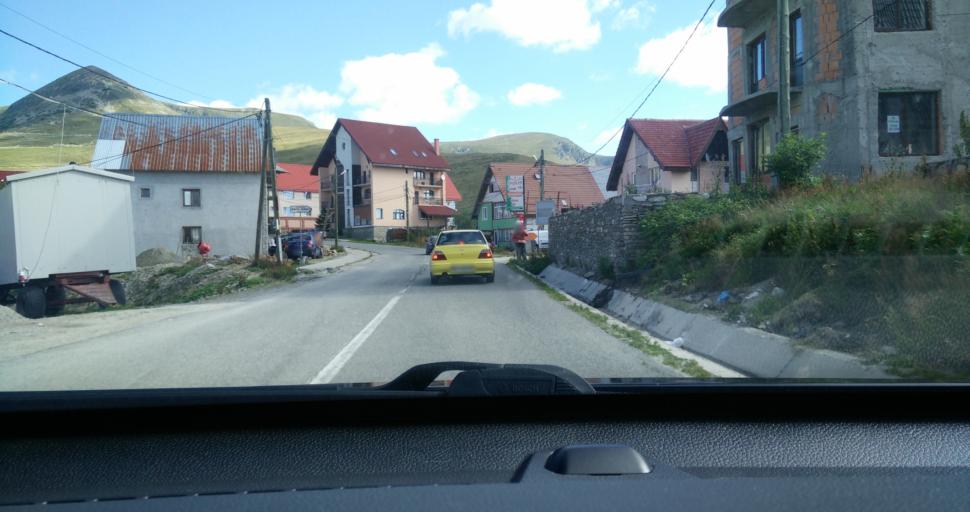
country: RO
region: Gorj
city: Novaci-Straini
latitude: 45.3051
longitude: 23.6844
